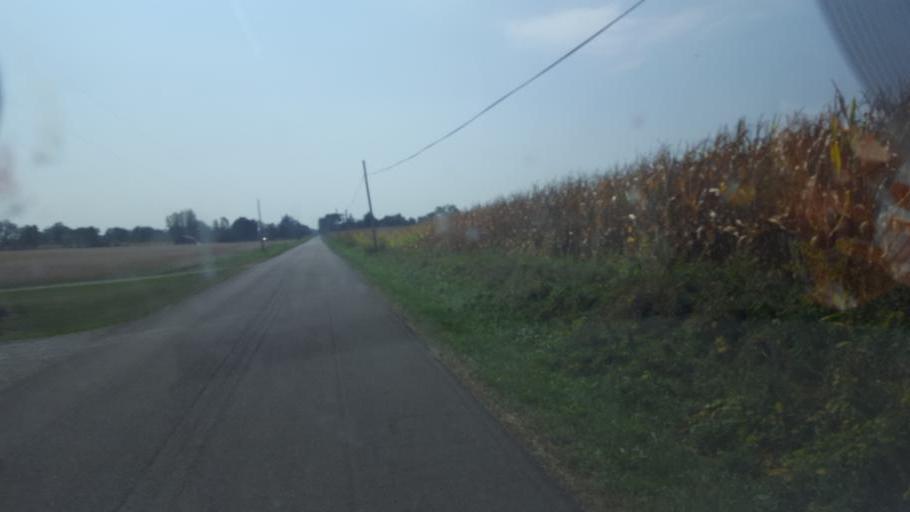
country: US
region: Ohio
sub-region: Morrow County
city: Mount Gilead
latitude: 40.5854
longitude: -82.8429
